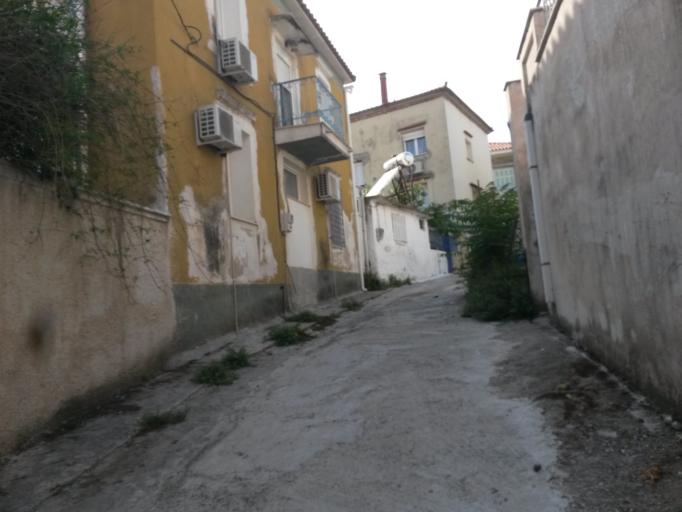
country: GR
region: North Aegean
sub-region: Nomos Lesvou
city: Moria
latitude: 39.1318
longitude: 26.5168
